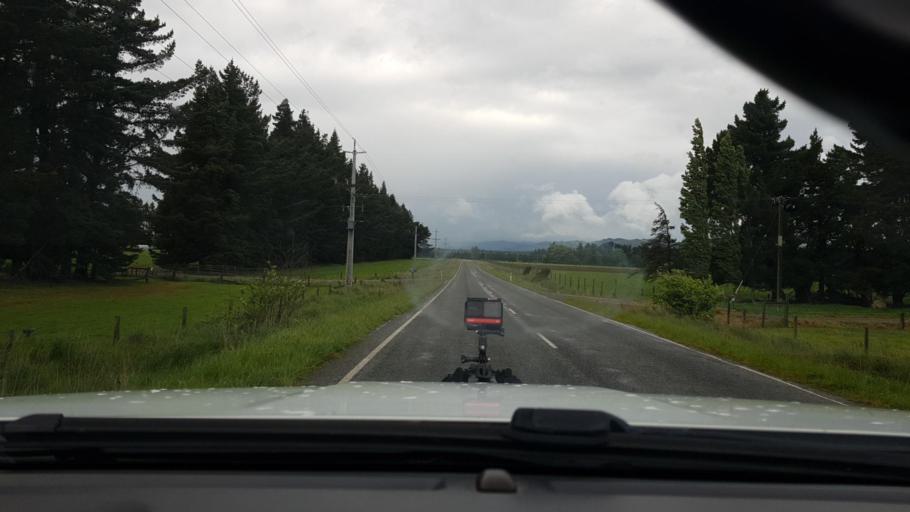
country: NZ
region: Southland
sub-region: Southland District
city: Winton
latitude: -45.7577
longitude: 168.4066
